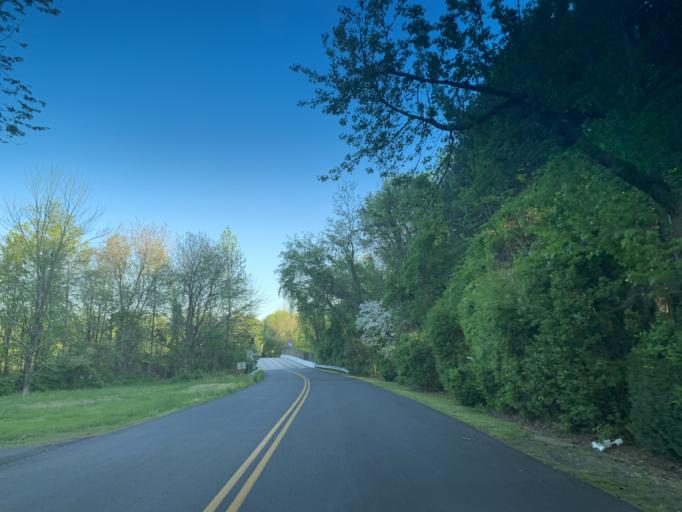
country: US
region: Maryland
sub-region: Harford County
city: Aberdeen
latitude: 39.5355
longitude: -76.1768
